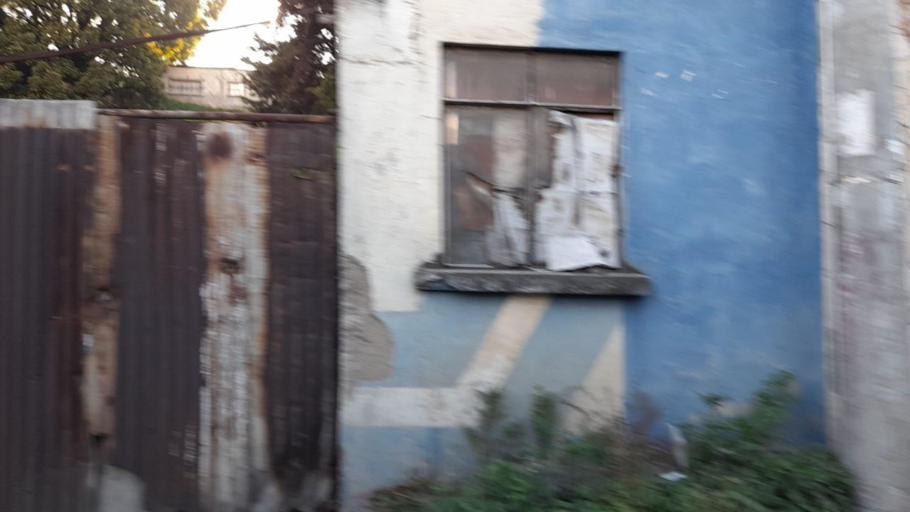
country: GT
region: Quetzaltenango
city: Quetzaltenango
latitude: 14.8378
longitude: -91.5145
